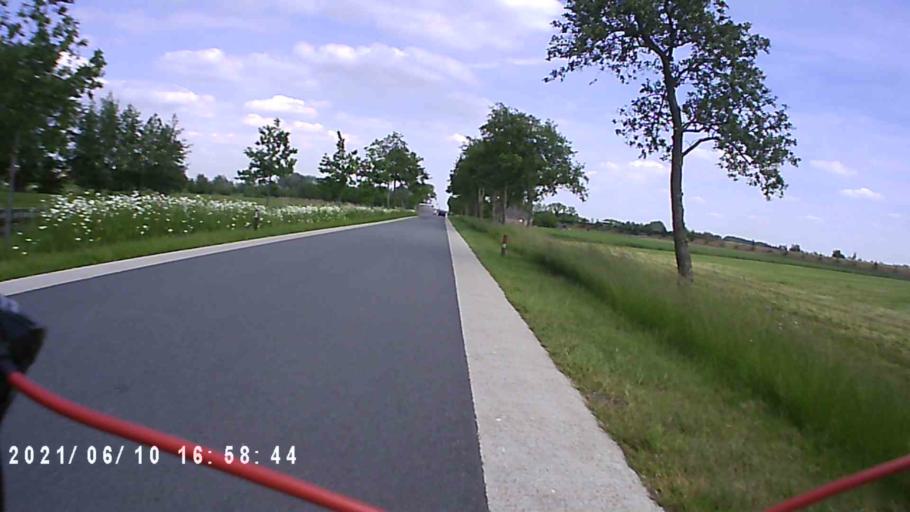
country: NL
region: Friesland
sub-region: Gemeente Kollumerland en Nieuwkruisland
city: Kollum
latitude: 53.2708
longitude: 6.1516
